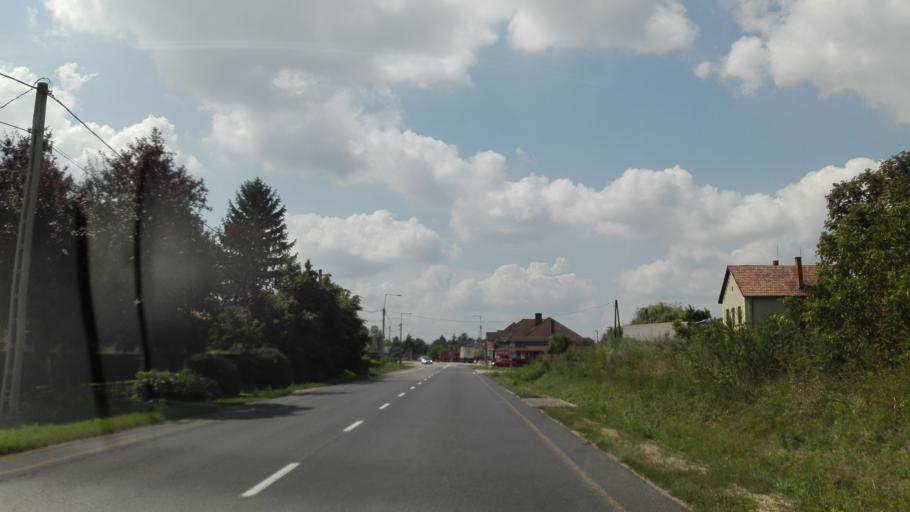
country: HU
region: Fejer
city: Eloszallas
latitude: 46.8321
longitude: 18.8335
